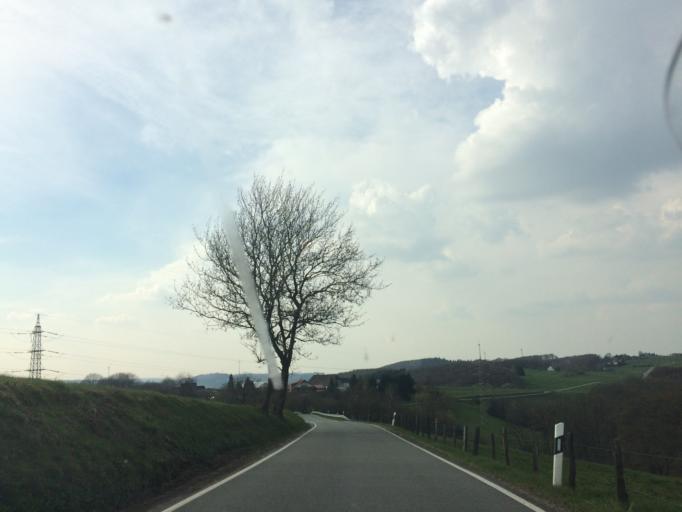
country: DE
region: North Rhine-Westphalia
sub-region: Regierungsbezirk Arnsberg
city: Nachrodt-Wiblingwerde
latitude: 51.3119
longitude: 7.6110
